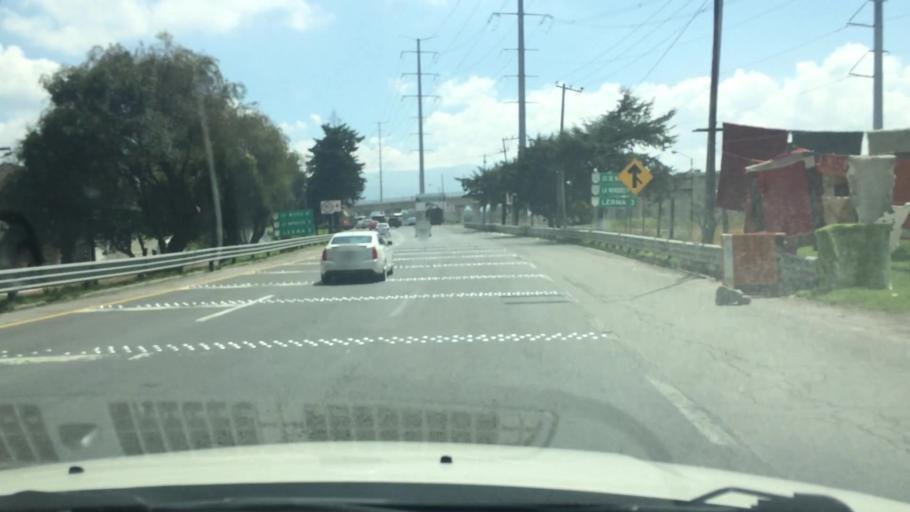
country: MX
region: Morelos
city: Lerma de Villada
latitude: 19.2798
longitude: -99.5100
